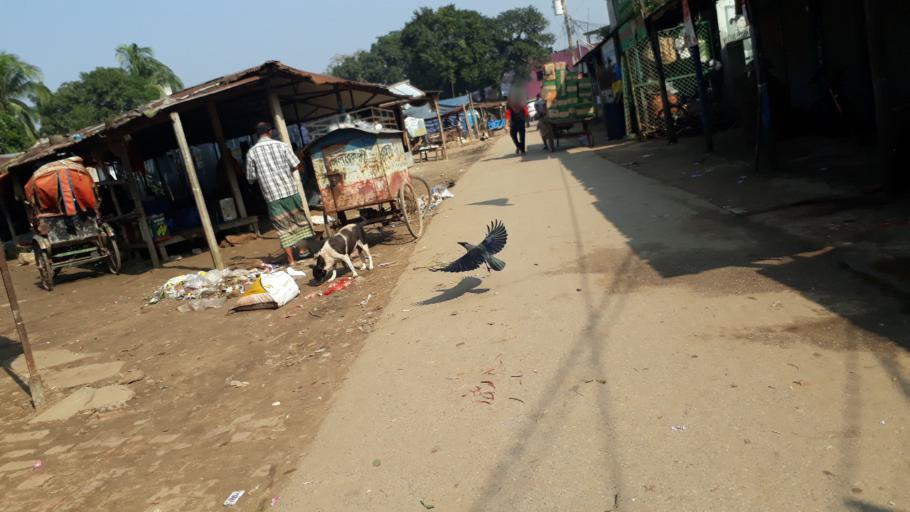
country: BD
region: Dhaka
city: Tungi
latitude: 23.8786
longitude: 90.2593
